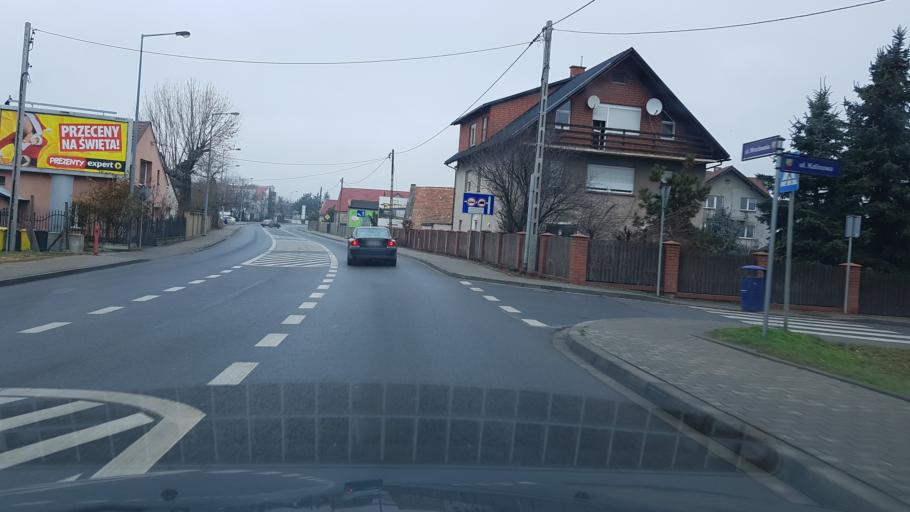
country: PL
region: Lower Silesian Voivodeship
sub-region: Powiat wroclawski
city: Bielany Wroclawskie
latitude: 51.0330
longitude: 16.9682
